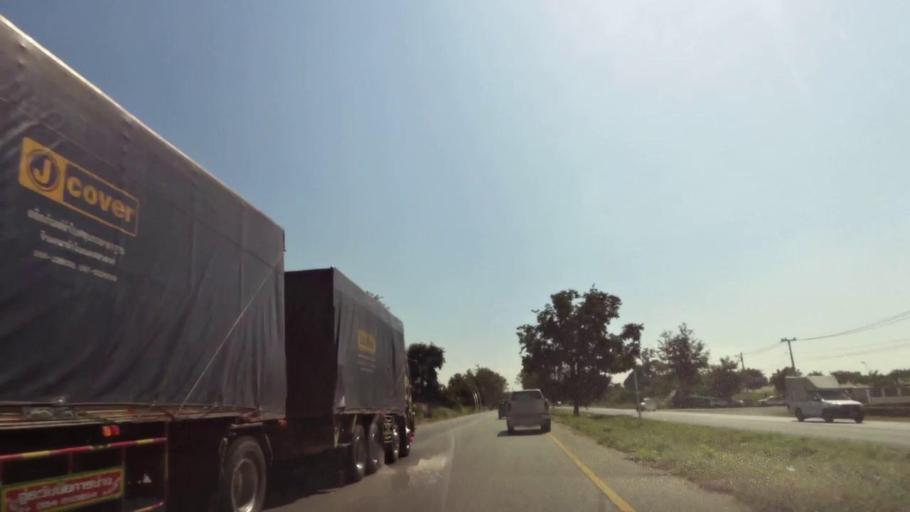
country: TH
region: Nakhon Sawan
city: Kao Liao
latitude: 15.8212
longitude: 100.1194
